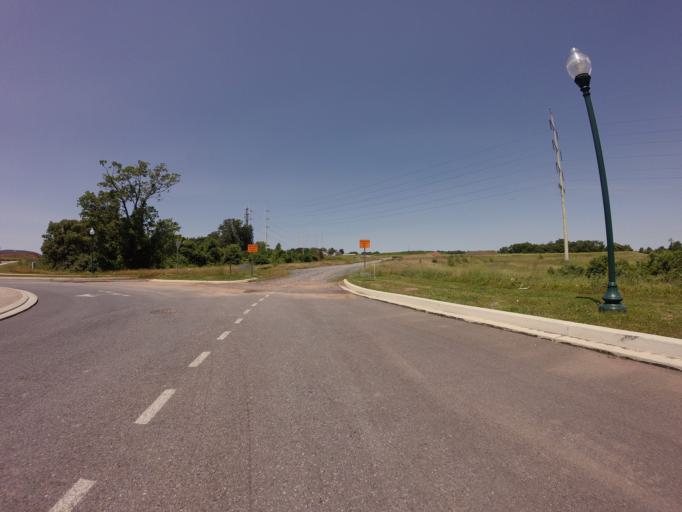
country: US
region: Maryland
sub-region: Frederick County
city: Ballenger Creek
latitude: 39.3948
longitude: -77.4489
